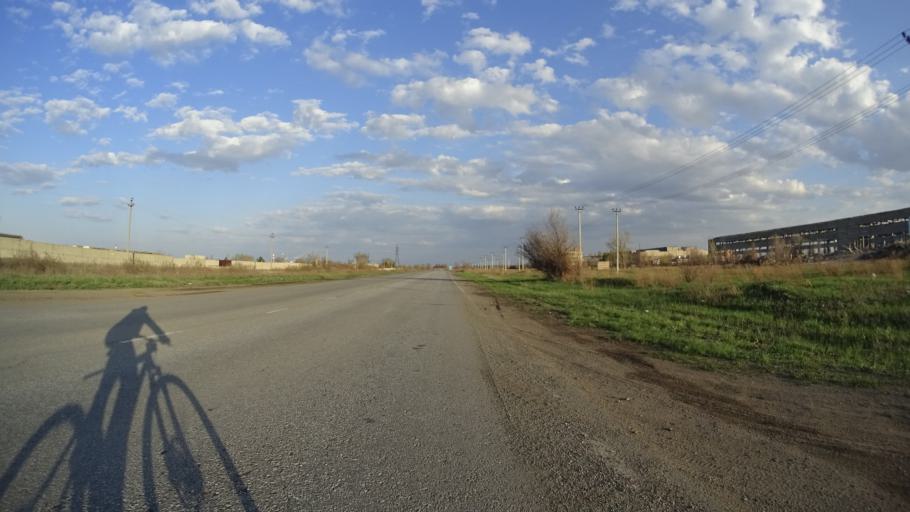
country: RU
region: Chelyabinsk
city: Troitsk
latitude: 54.0663
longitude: 61.5666
